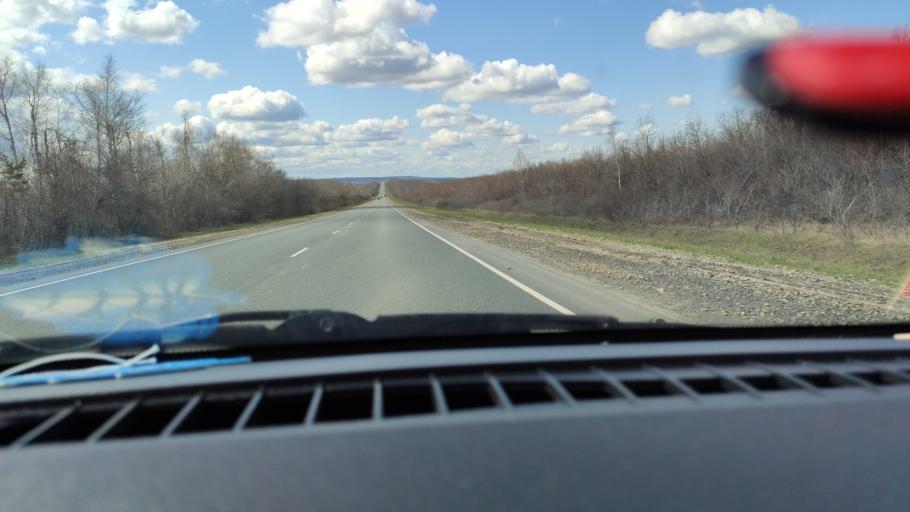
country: RU
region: Saratov
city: Khvalynsk
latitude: 52.6114
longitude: 48.1595
